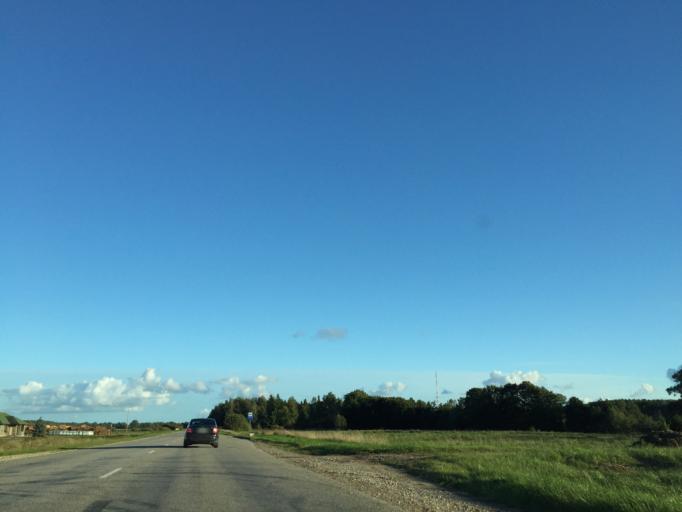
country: LV
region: Kuldigas Rajons
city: Kuldiga
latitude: 56.9564
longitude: 22.0064
